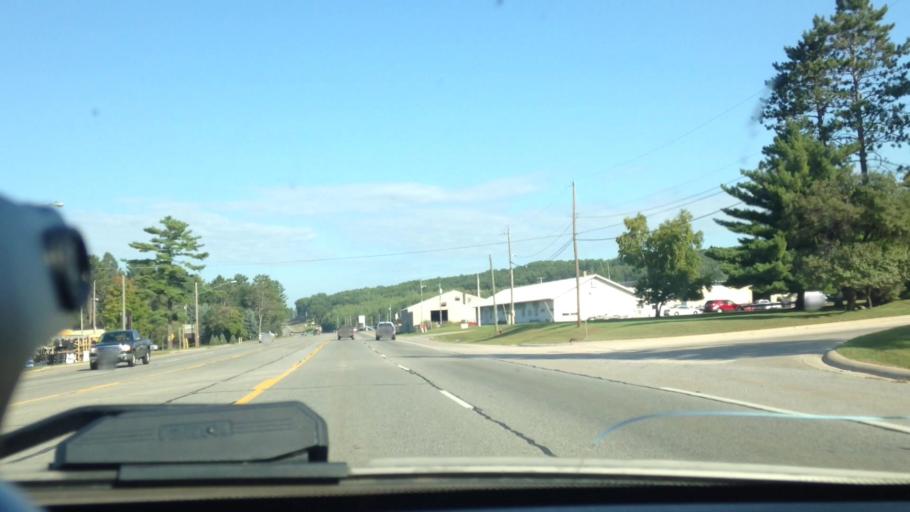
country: US
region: Michigan
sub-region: Dickinson County
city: Iron Mountain
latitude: 45.8479
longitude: -88.0509
